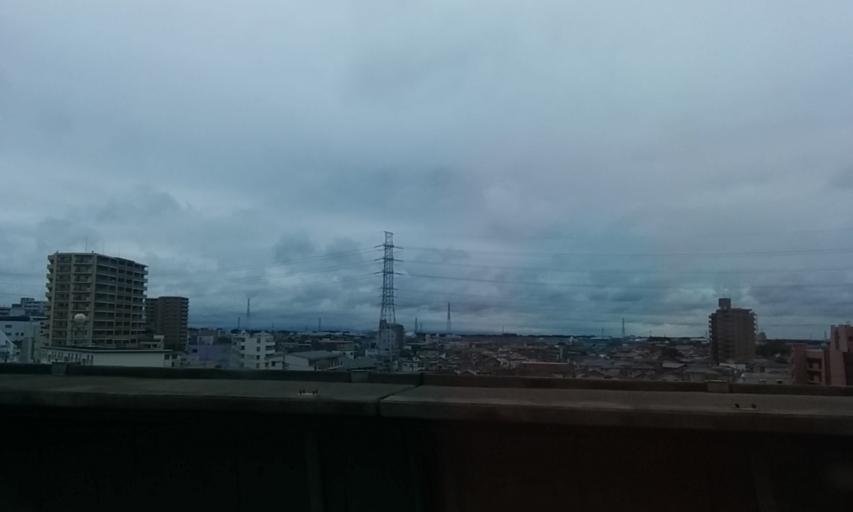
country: JP
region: Tochigi
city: Oyama
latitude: 36.3087
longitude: 139.8036
